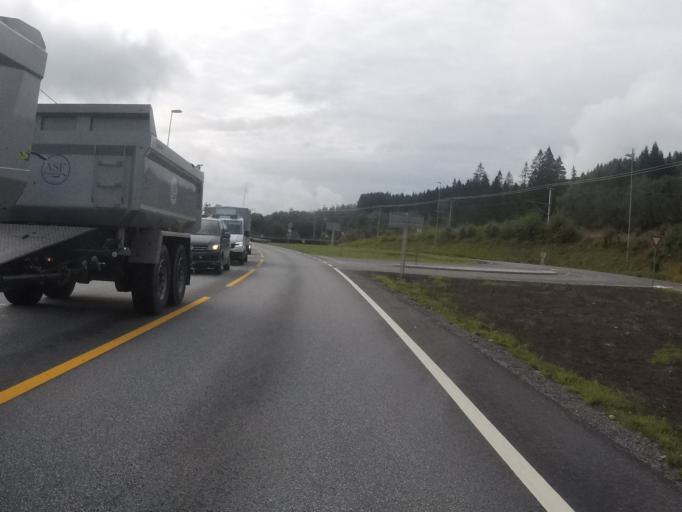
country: NO
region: Rogaland
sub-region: Lund
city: Moi
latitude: 58.4623
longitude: 6.5313
